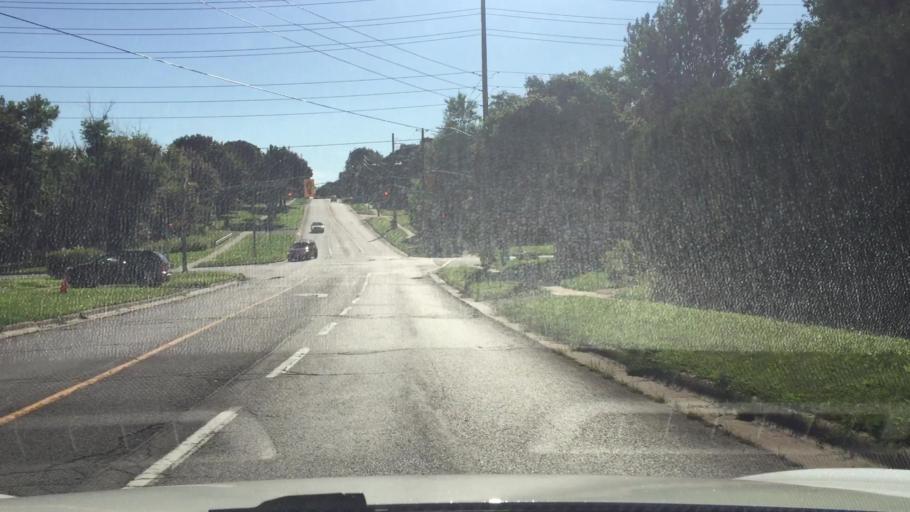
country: CA
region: Ontario
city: Oshawa
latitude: 43.9096
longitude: -78.8464
